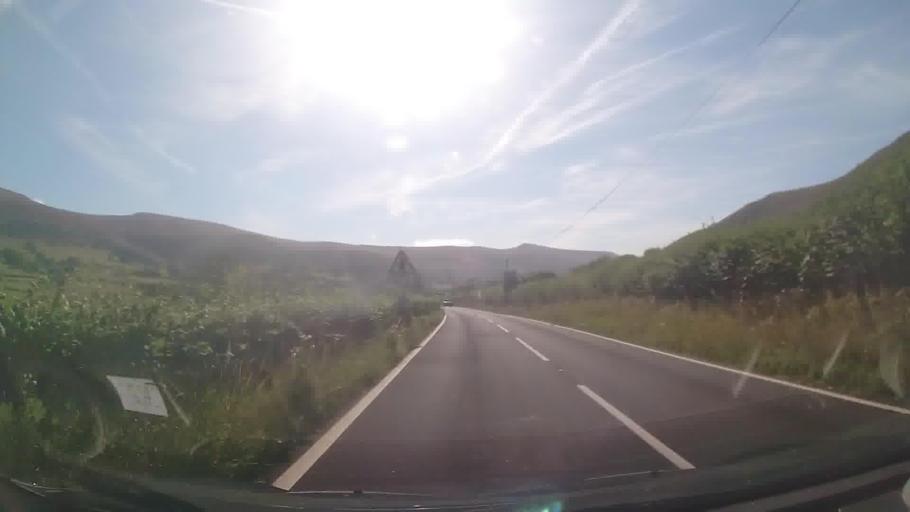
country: GB
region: Wales
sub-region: Sir Powys
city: Hay
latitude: 51.9538
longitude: -3.1977
